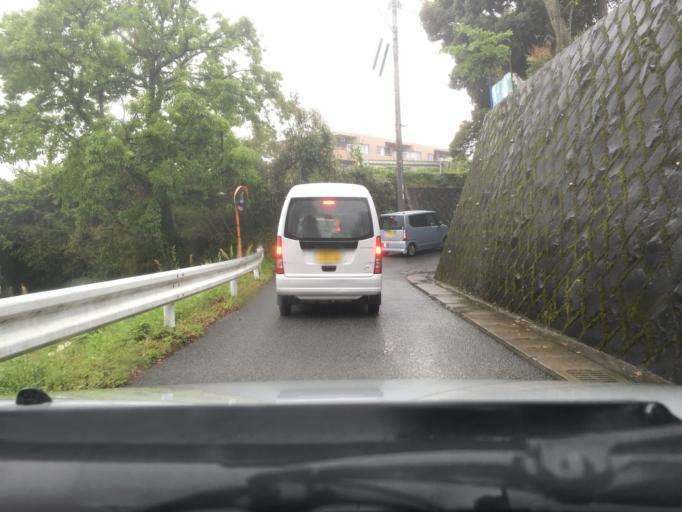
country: JP
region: Kumamoto
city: Ueki
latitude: 32.8728
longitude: 130.7007
